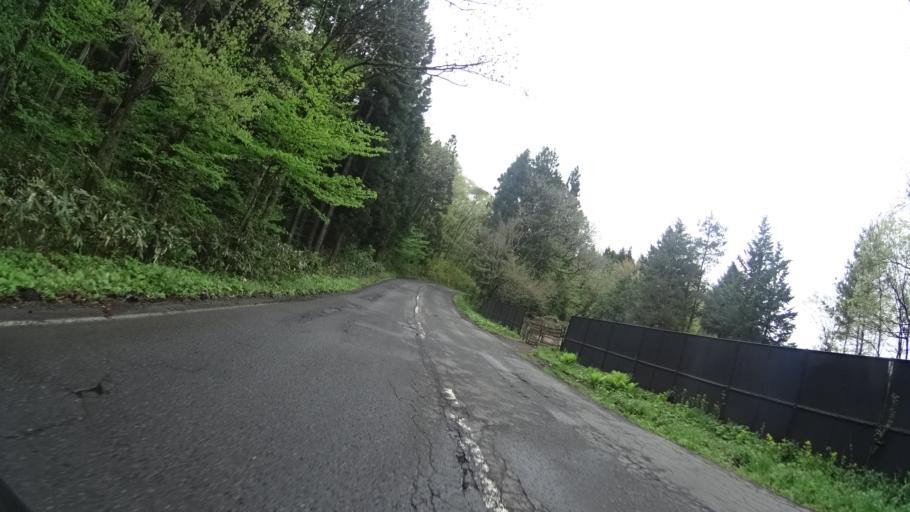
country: JP
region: Nagano
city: Nagano-shi
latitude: 36.7522
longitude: 138.2023
